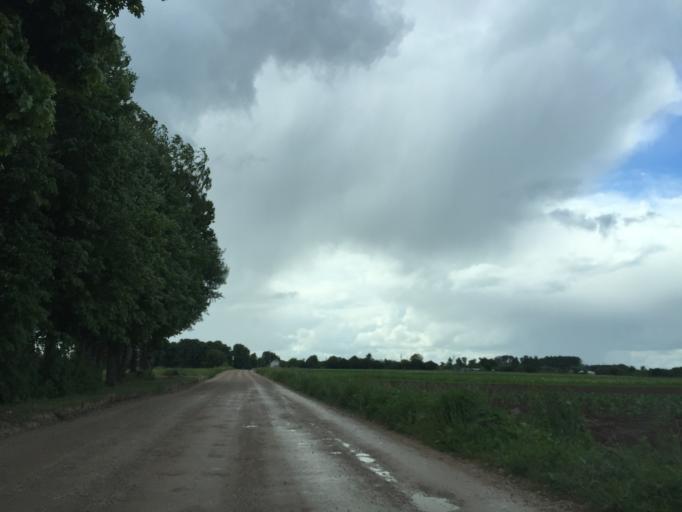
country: LV
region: Lecava
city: Iecava
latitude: 56.6037
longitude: 24.1844
